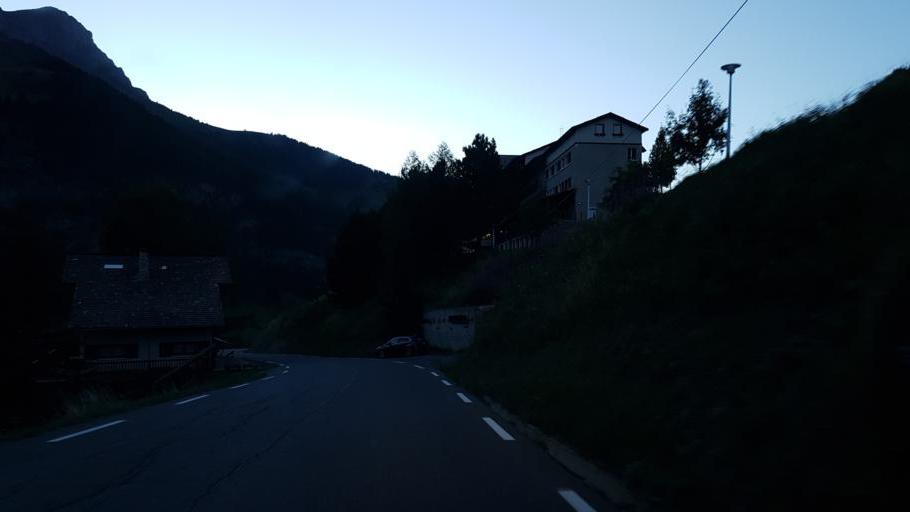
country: IT
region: Piedmont
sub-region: Provincia di Cuneo
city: Pontechianale
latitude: 44.7031
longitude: 6.8567
